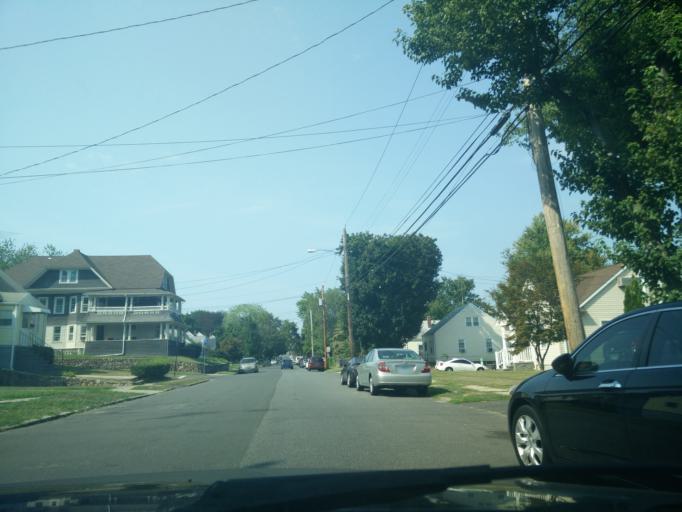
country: US
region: Connecticut
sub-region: Fairfield County
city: Trumbull
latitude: 41.2076
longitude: -73.2155
